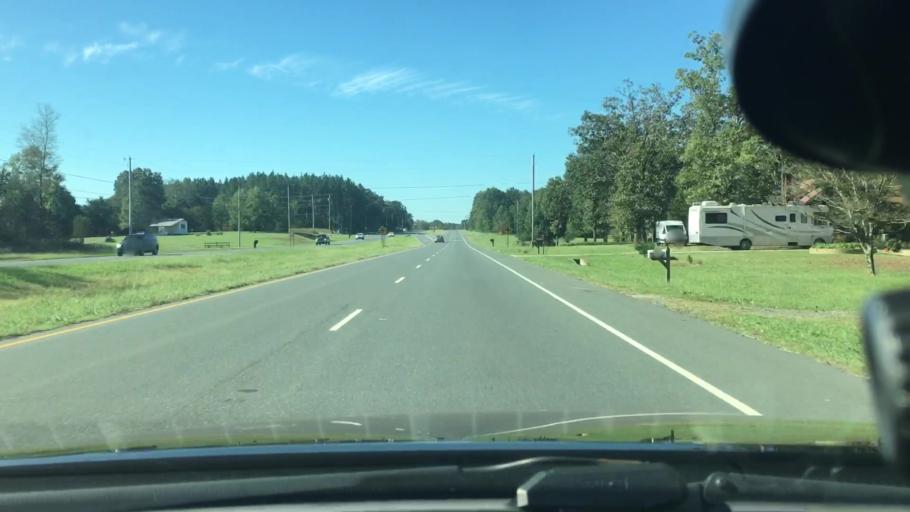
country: US
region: North Carolina
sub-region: Stanly County
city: Oakboro
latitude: 35.2983
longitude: -80.2834
